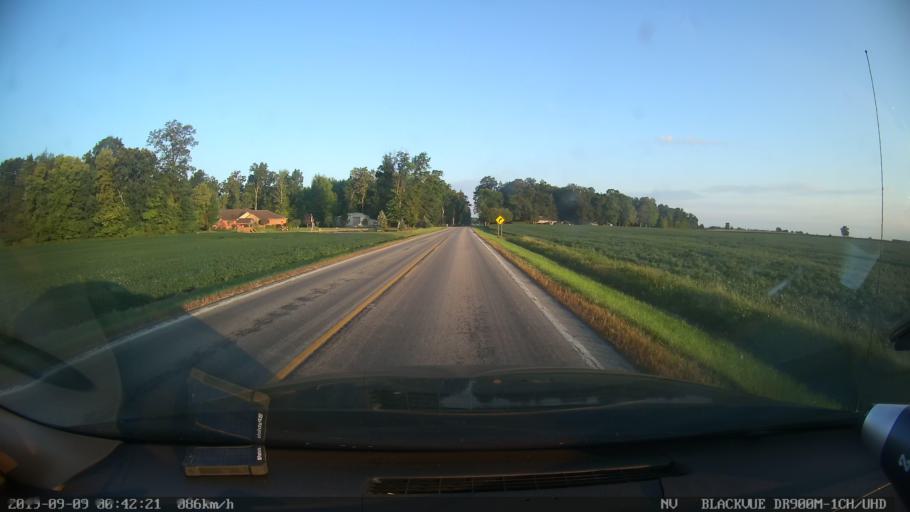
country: US
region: Ohio
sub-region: Crawford County
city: Bucyrus
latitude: 40.7638
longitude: -82.9187
